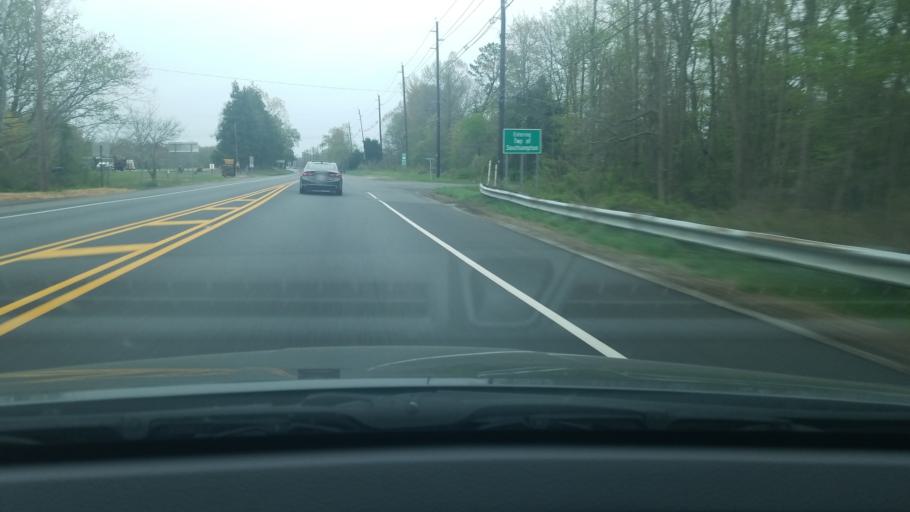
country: US
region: New Jersey
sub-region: Burlington County
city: Medford Lakes
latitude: 39.8983
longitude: -74.7879
